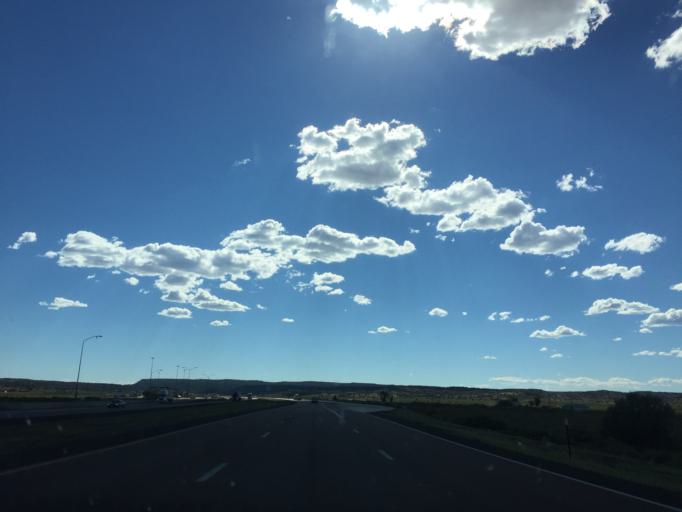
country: US
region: New Mexico
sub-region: McKinley County
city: Gallup
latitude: 35.4884
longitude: -108.8954
